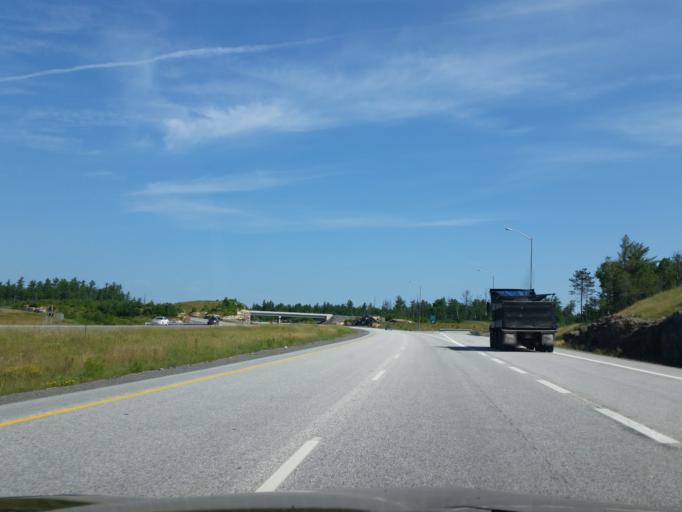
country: CA
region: Ontario
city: Greater Sudbury
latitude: 46.2234
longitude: -80.7704
